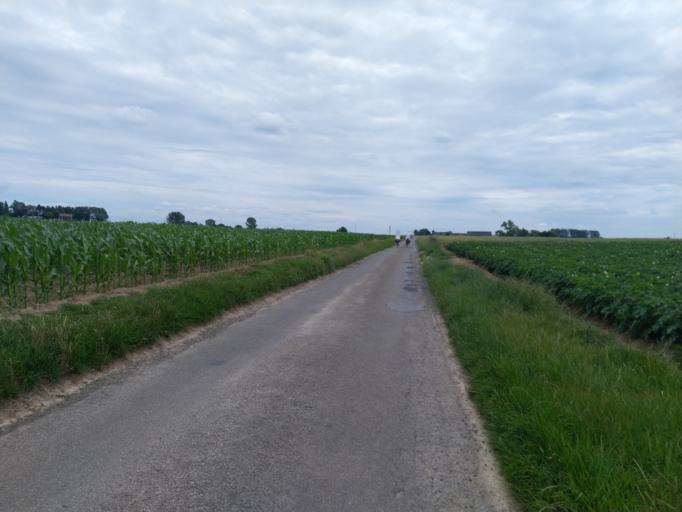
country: BE
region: Wallonia
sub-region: Province du Hainaut
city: Chievres
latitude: 50.5389
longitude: 3.8171
